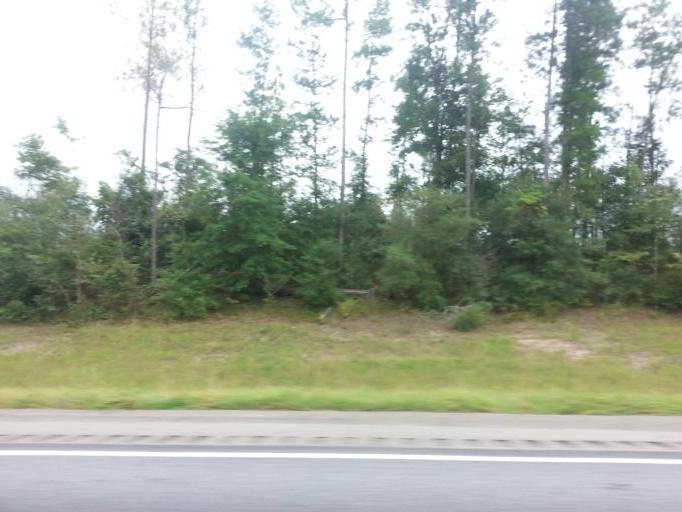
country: US
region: Alabama
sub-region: Conecuh County
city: Evergreen
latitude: 31.3226
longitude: -87.1378
